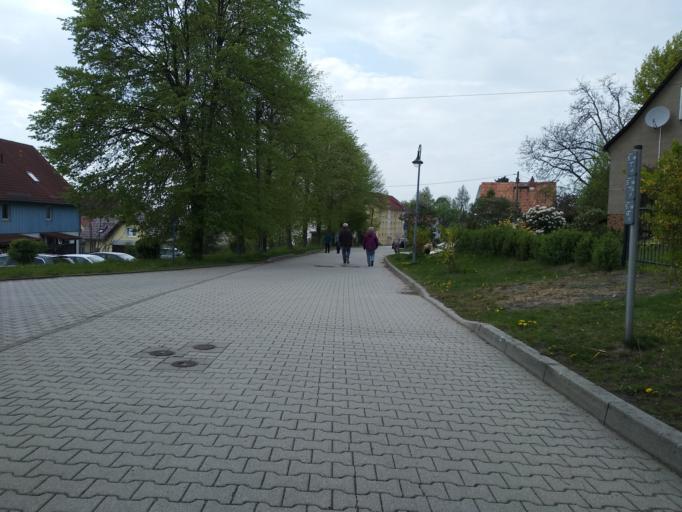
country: DE
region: Saxony
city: Hohnstein
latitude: 50.9746
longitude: 14.1146
